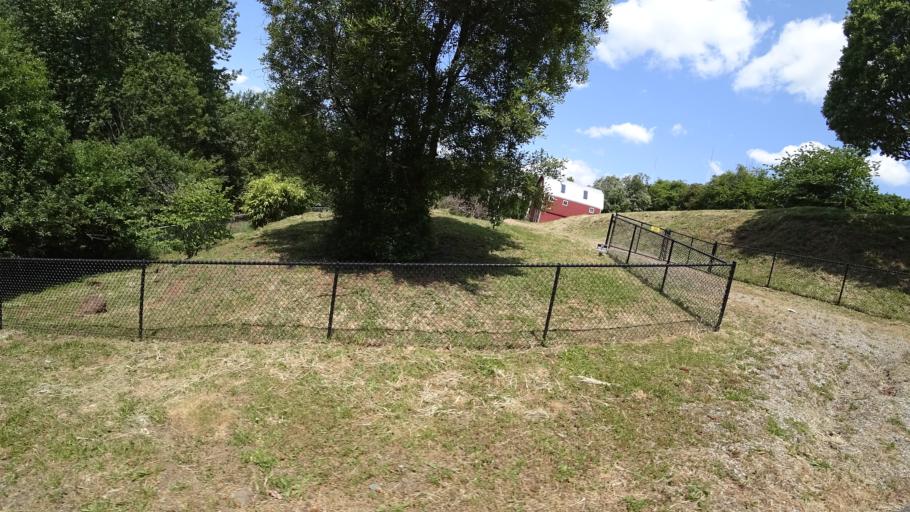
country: US
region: Oregon
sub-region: Clackamas County
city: Happy Valley
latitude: 45.4504
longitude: -122.5504
